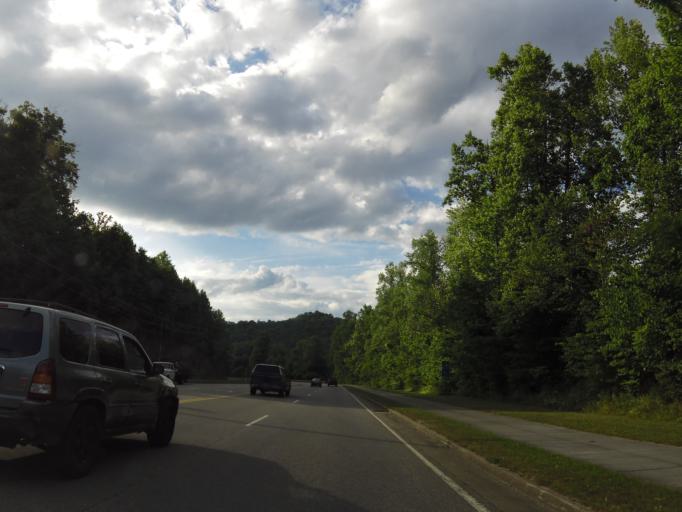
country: US
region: Tennessee
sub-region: Blount County
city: Wildwood
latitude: 35.6767
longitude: -83.7672
